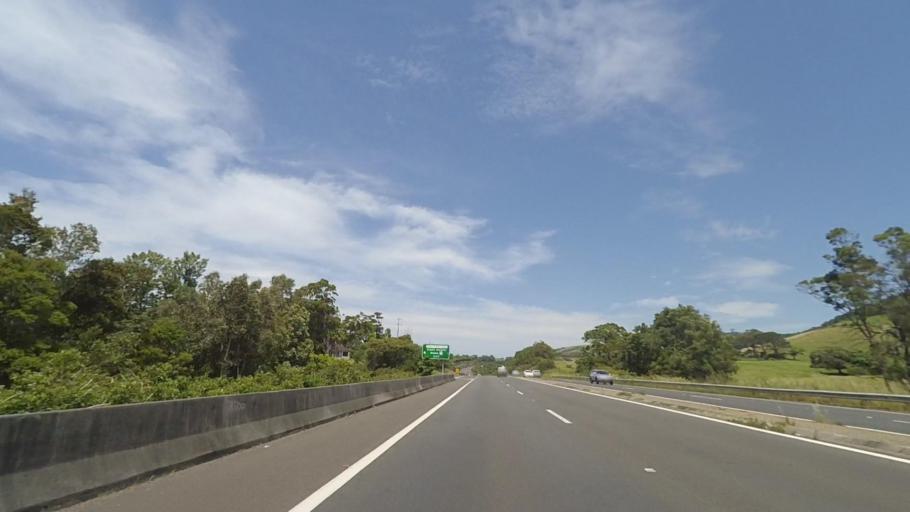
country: AU
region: New South Wales
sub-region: Kiama
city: Kiama
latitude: -34.6859
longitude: 150.8442
